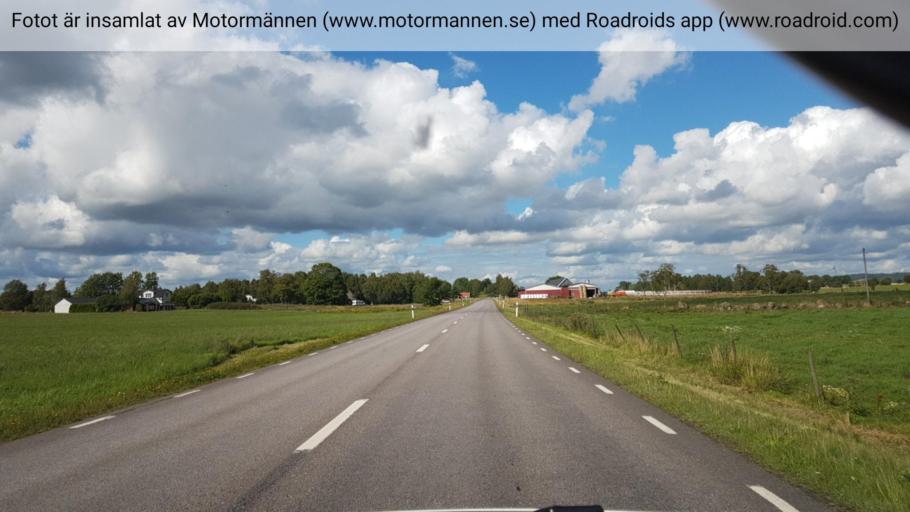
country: SE
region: Vaestra Goetaland
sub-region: Falkopings Kommun
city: Falkoeping
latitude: 58.0927
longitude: 13.5240
